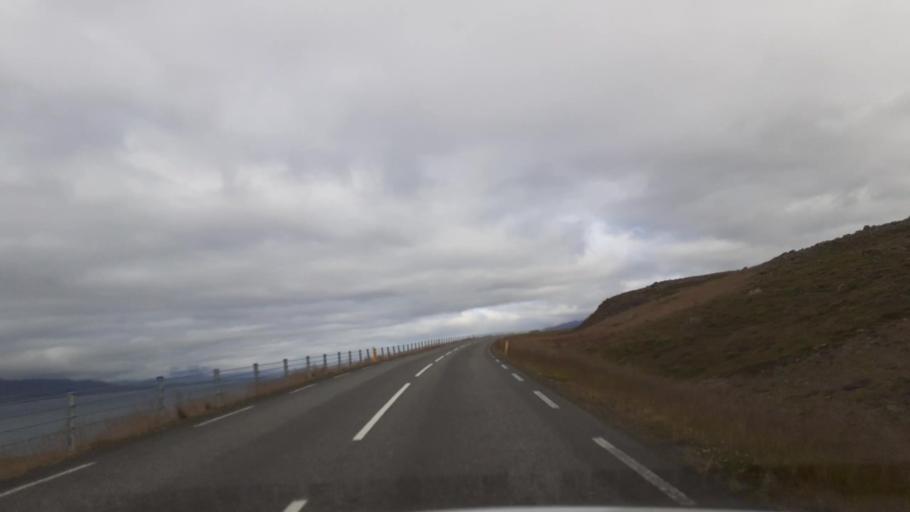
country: IS
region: Northeast
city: Akureyri
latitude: 65.8247
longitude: -18.0556
